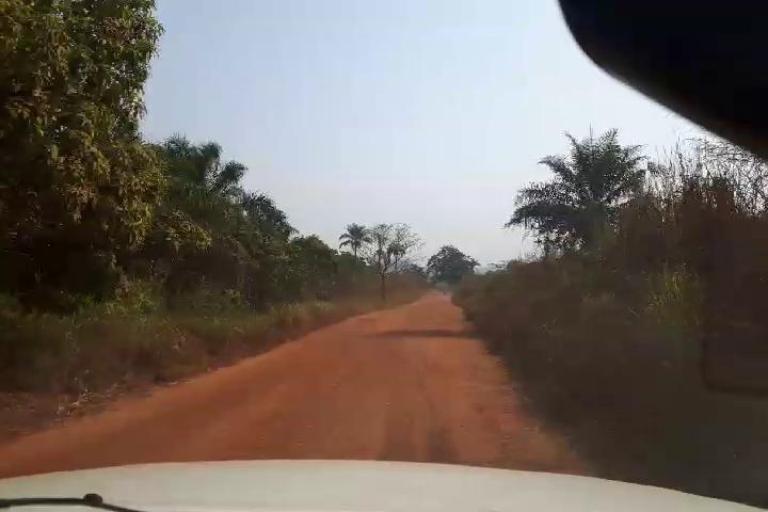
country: SL
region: Northern Province
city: Masingbi
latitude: 8.8514
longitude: -11.8274
